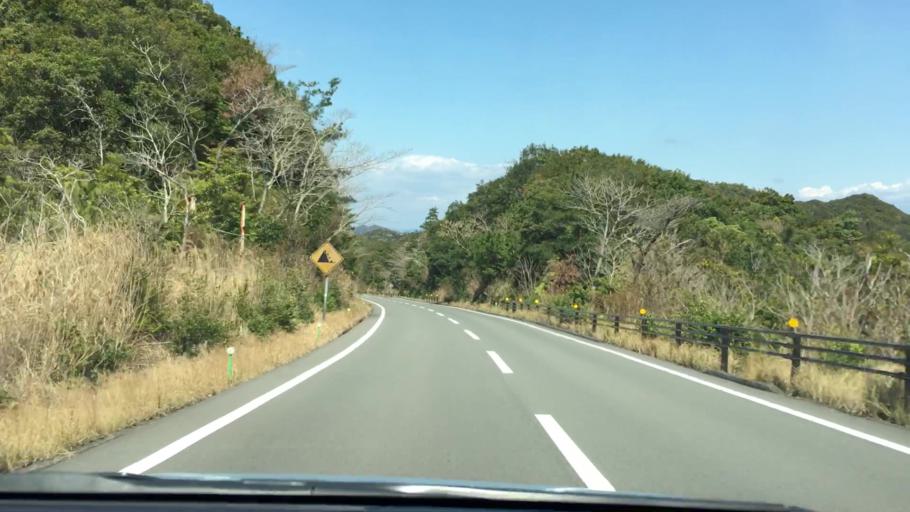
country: JP
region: Mie
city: Toba
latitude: 34.4349
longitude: 136.9124
